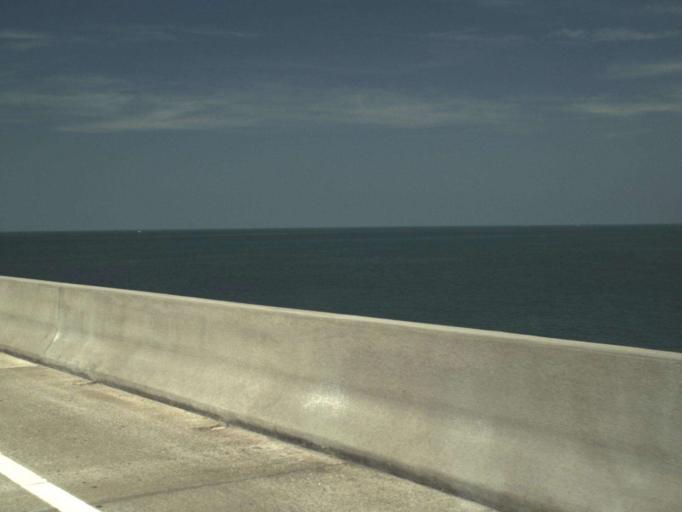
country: US
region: Florida
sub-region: Monroe County
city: Marathon
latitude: 24.7994
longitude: -80.8614
